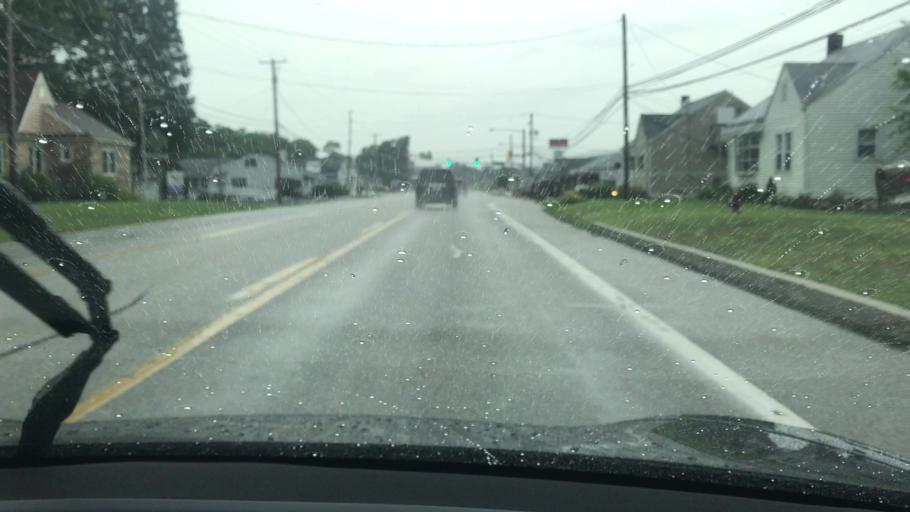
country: US
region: Pennsylvania
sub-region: Dauphin County
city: Lawrence Park
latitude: 40.3367
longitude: -76.8187
